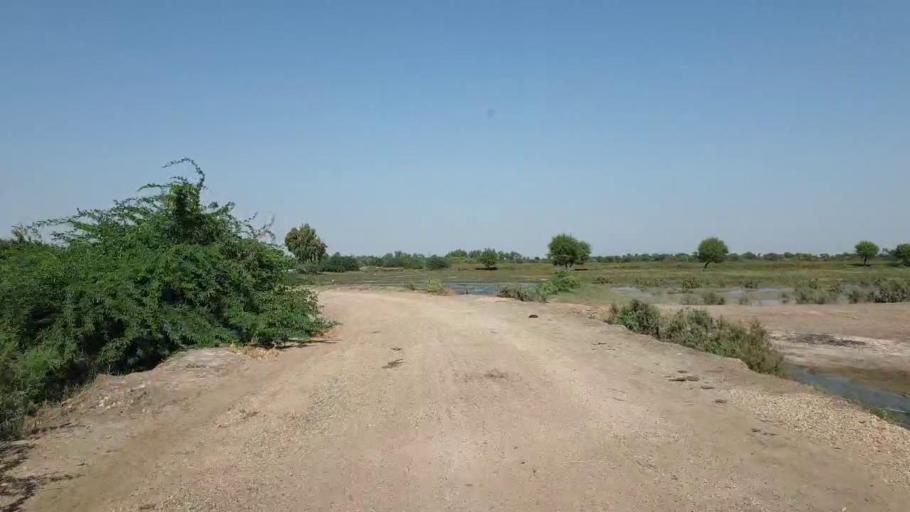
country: PK
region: Sindh
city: Tando Bago
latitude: 24.7355
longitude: 69.0431
